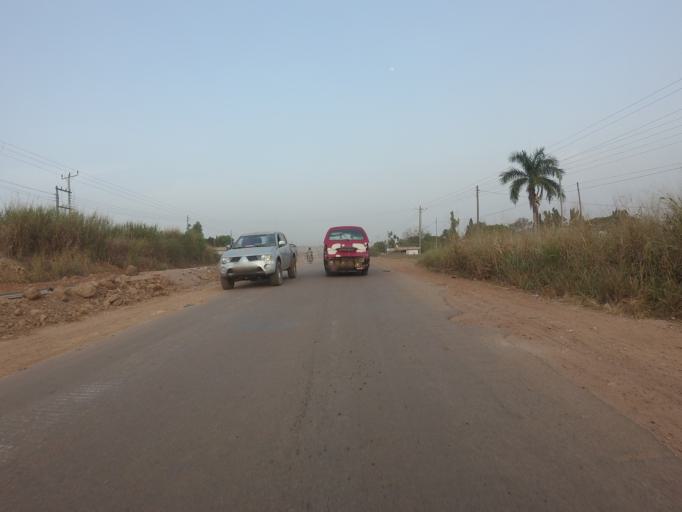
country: GH
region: Volta
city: Ho
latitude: 6.5930
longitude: 0.4358
